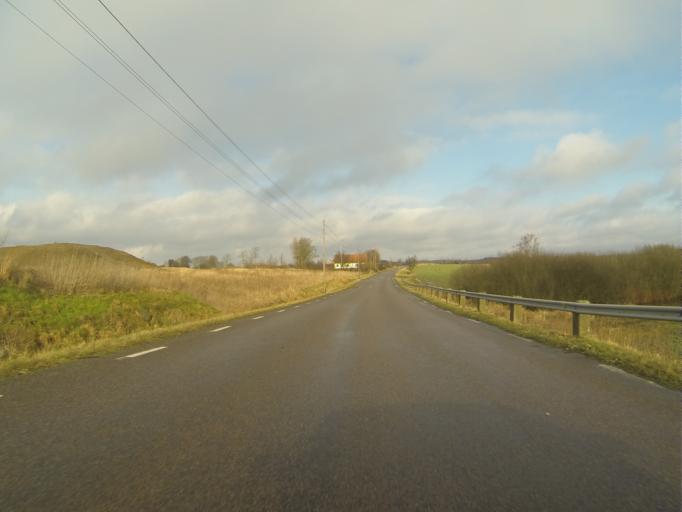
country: SE
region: Skane
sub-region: Svedala Kommun
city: Svedala
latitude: 55.5110
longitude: 13.2651
